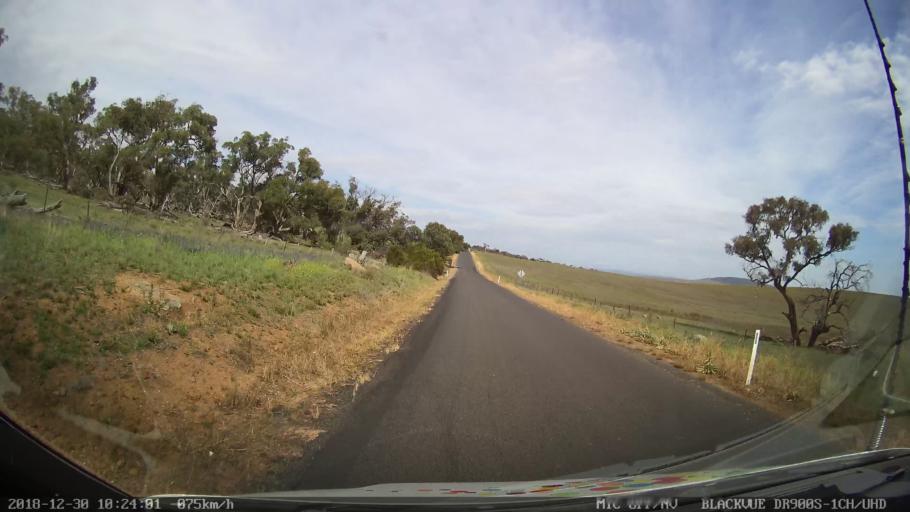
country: AU
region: New South Wales
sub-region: Snowy River
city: Berridale
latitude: -36.5328
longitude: 148.9757
